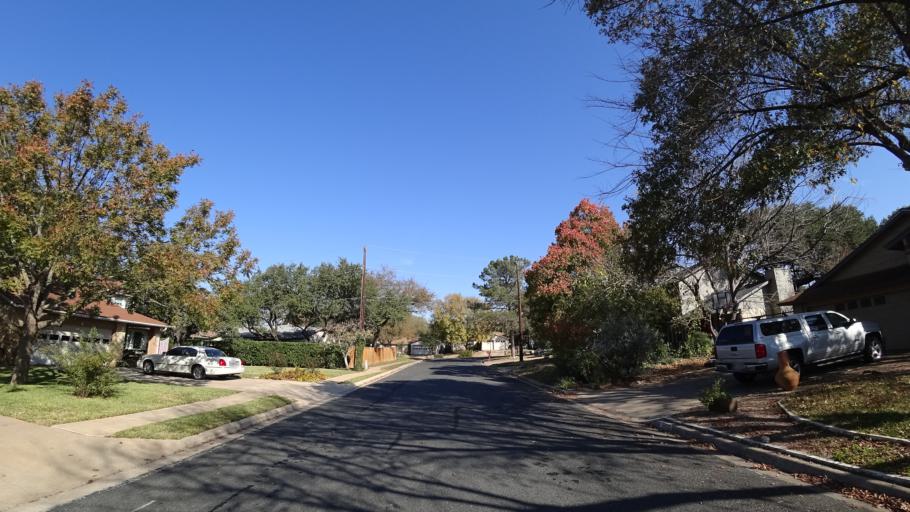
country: US
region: Texas
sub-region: Travis County
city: Barton Creek
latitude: 30.2318
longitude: -97.8530
